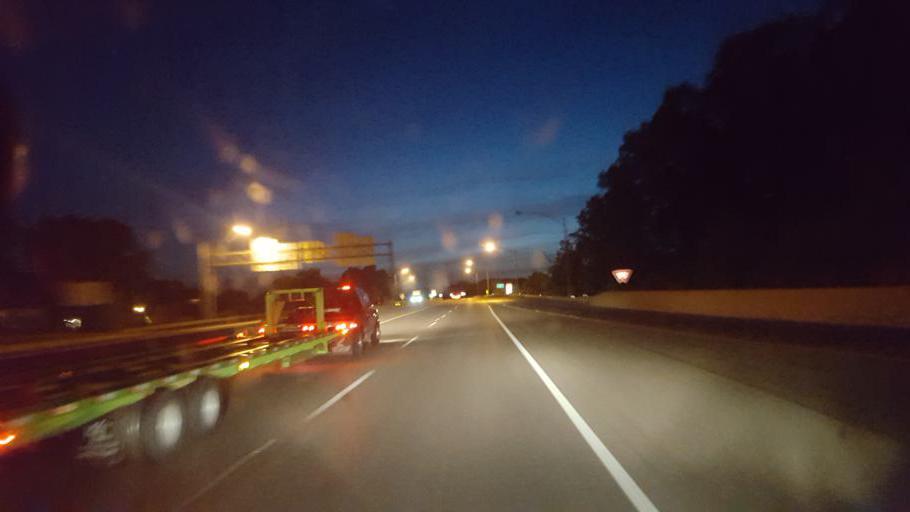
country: US
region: Ohio
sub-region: Muskingum County
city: Zanesville
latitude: 39.9484
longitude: -82.0199
